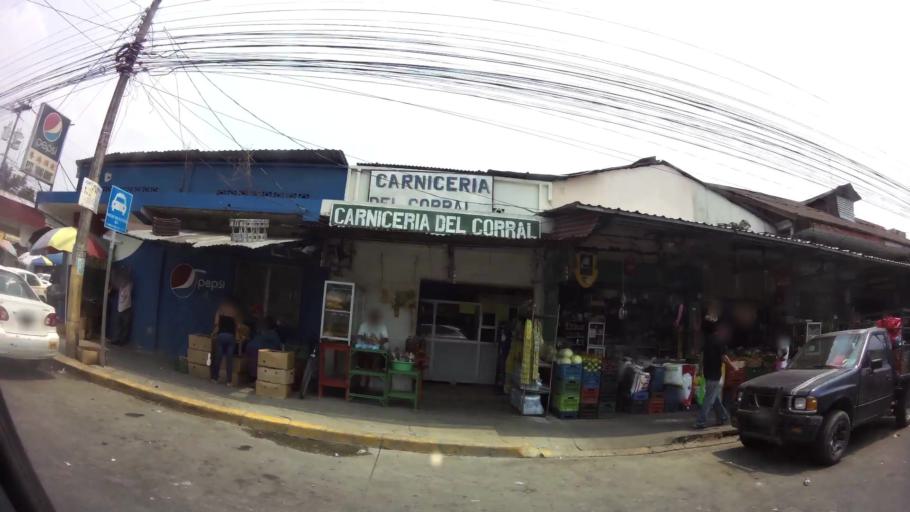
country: HN
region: Yoro
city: El Progreso
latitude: 15.4009
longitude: -87.8077
